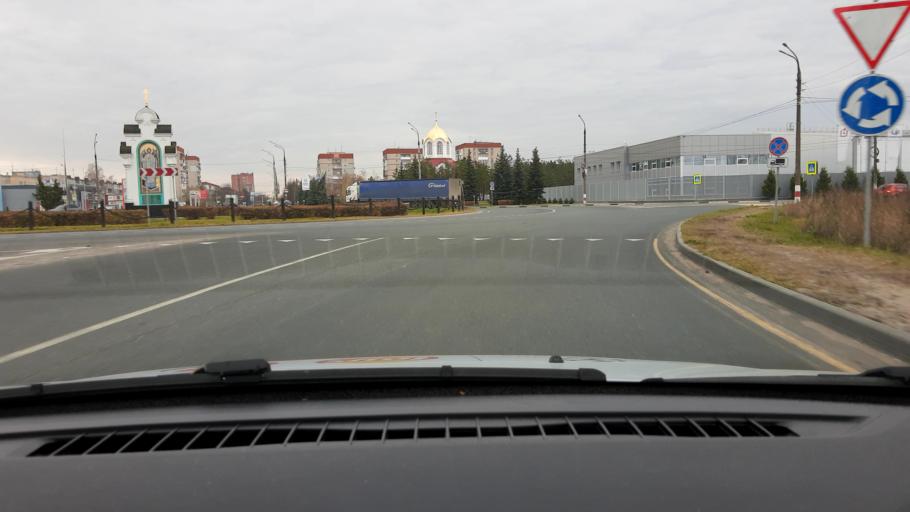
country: RU
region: Nizjnij Novgorod
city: Dzerzhinsk
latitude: 56.2584
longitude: 43.4676
